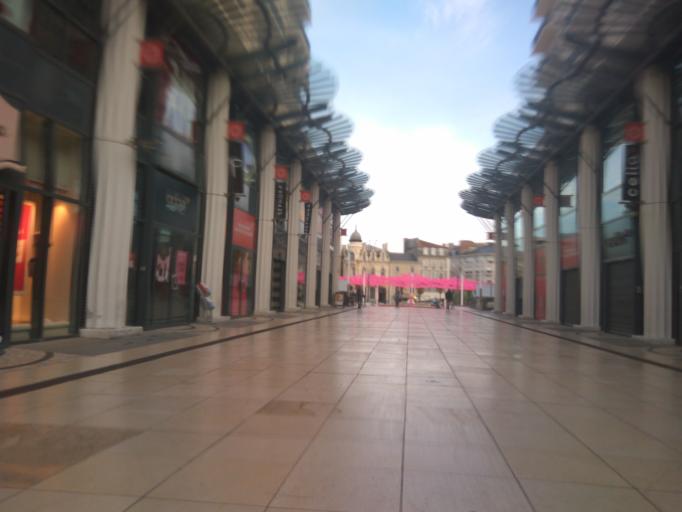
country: FR
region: Aquitaine
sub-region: Departement des Pyrenees-Atlantiques
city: Pau
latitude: 43.2949
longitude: -0.3684
